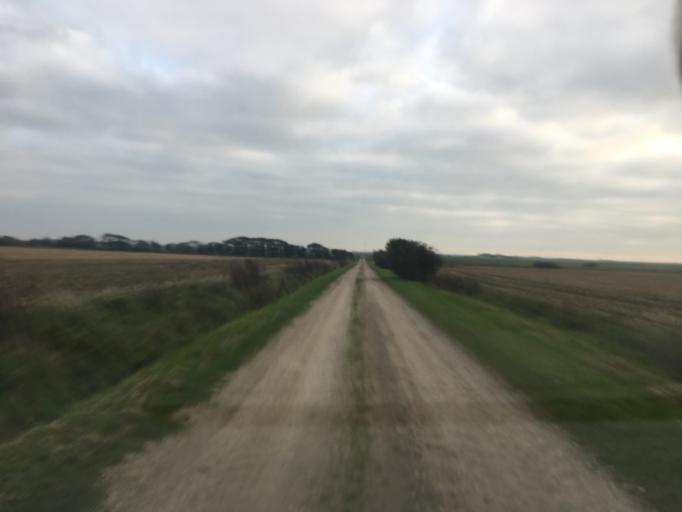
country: DE
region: Schleswig-Holstein
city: Rodenas
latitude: 54.9618
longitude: 8.7387
